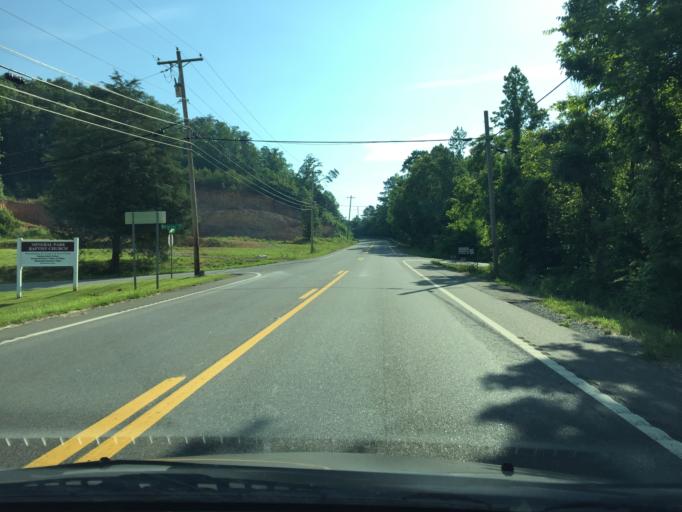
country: US
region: Tennessee
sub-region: Hamilton County
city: Collegedale
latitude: 35.0885
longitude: -85.0127
